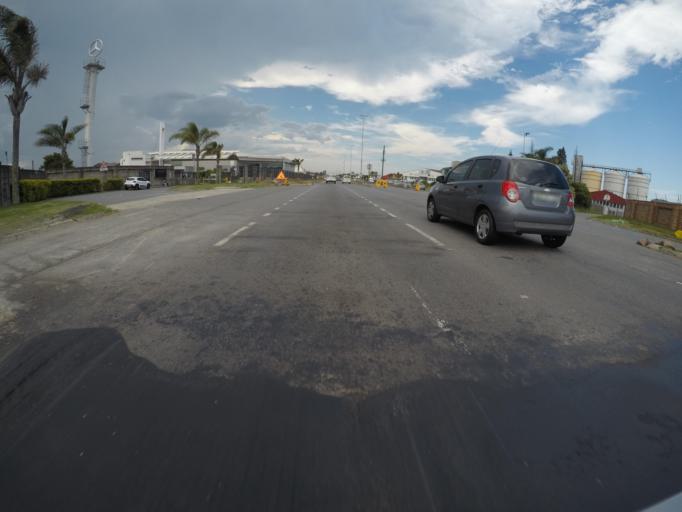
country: ZA
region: Eastern Cape
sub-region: Buffalo City Metropolitan Municipality
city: East London
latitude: -33.0311
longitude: 27.8853
